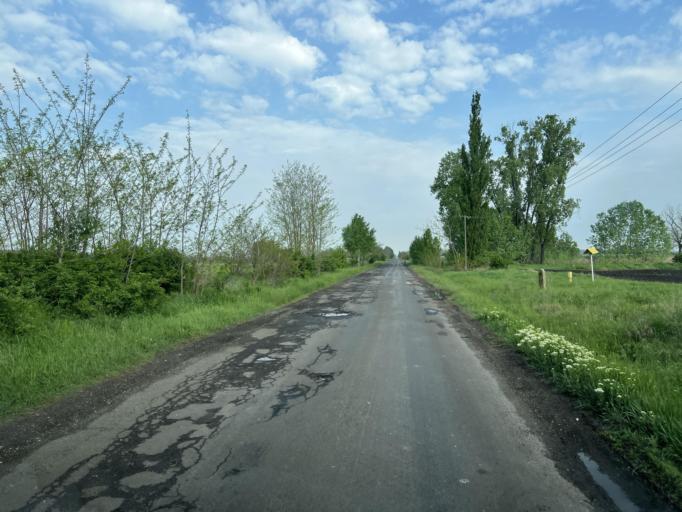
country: HU
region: Pest
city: Abony
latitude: 47.1569
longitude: 20.0514
